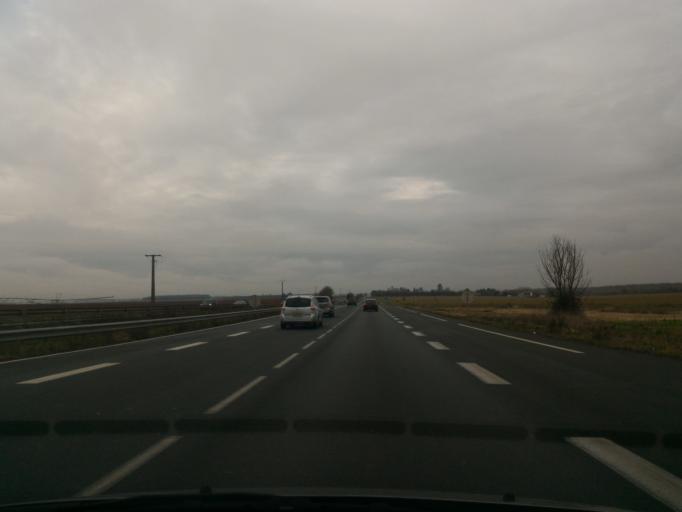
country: FR
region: Poitou-Charentes
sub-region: Departement de la Vienne
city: Vivonne
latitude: 46.3958
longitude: 0.2291
